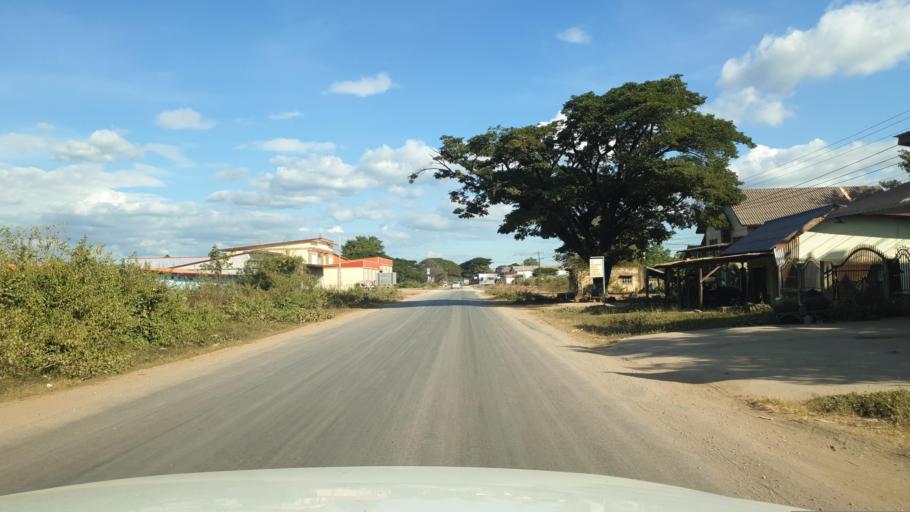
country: LA
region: Khammouan
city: Thakhek
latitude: 17.3817
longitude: 104.8436
